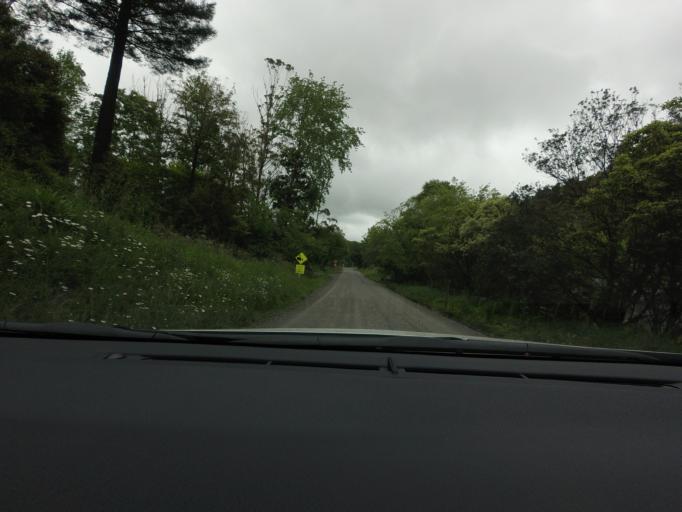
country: NZ
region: Auckland
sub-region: Auckland
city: Warkworth
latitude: -36.4792
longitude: 174.5616
